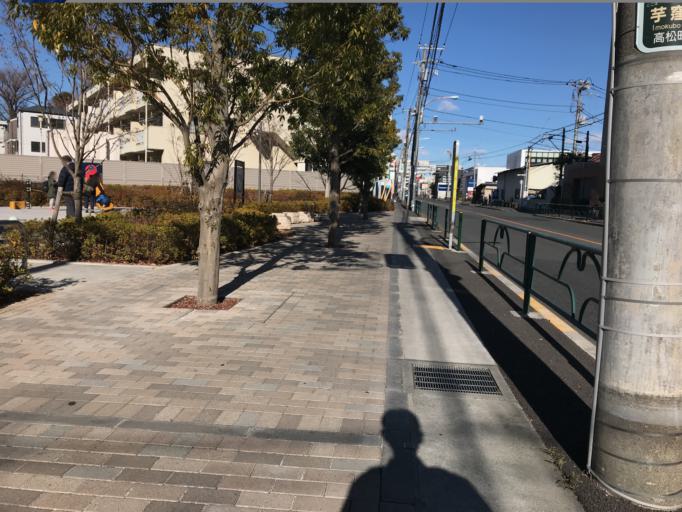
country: JP
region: Tokyo
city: Hino
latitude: 35.7095
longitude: 139.4219
